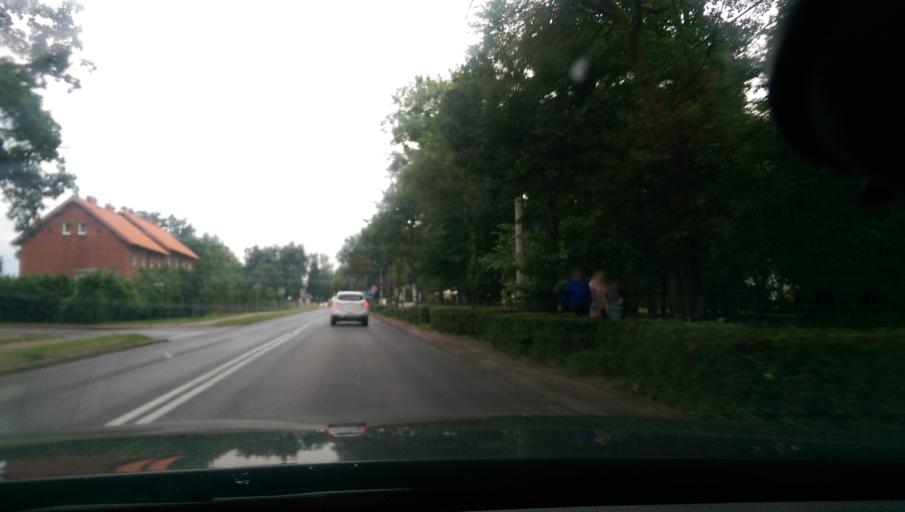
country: PL
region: Warmian-Masurian Voivodeship
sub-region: Powiat szczycienski
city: Szczytno
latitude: 53.5589
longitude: 20.9891
